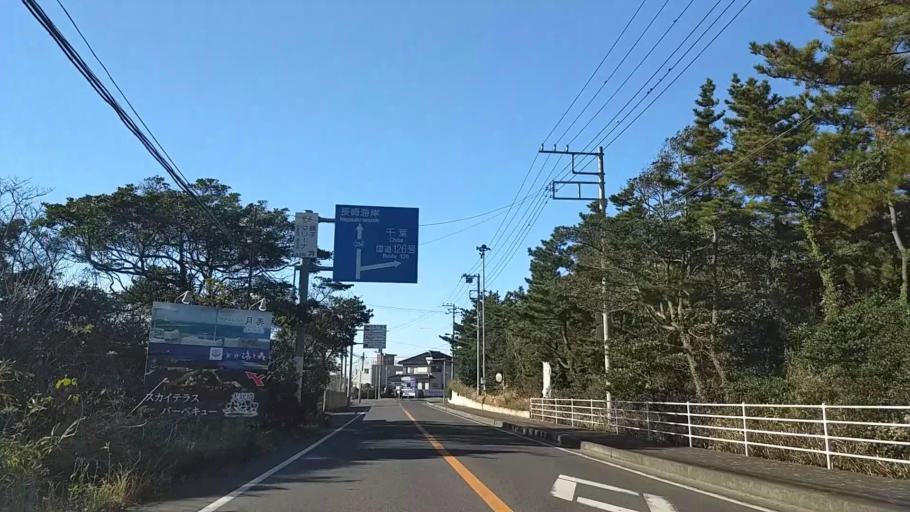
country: JP
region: Chiba
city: Hasaki
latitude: 35.7063
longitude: 140.8631
